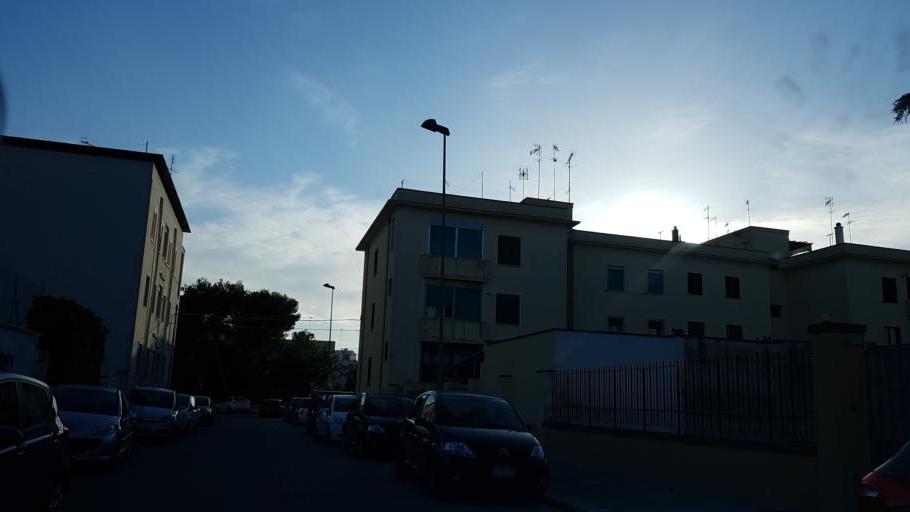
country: IT
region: Apulia
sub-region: Provincia di Brindisi
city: Materdomini
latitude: 40.6460
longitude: 17.9471
